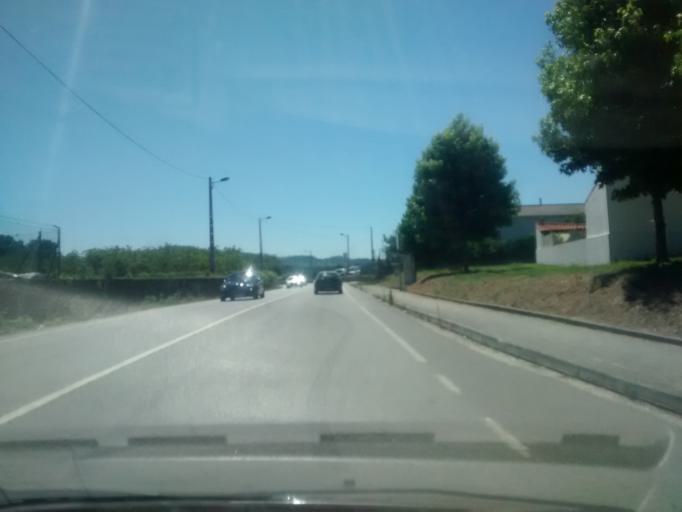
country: PT
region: Braga
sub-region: Barcelos
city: Galegos
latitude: 41.5300
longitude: -8.5572
